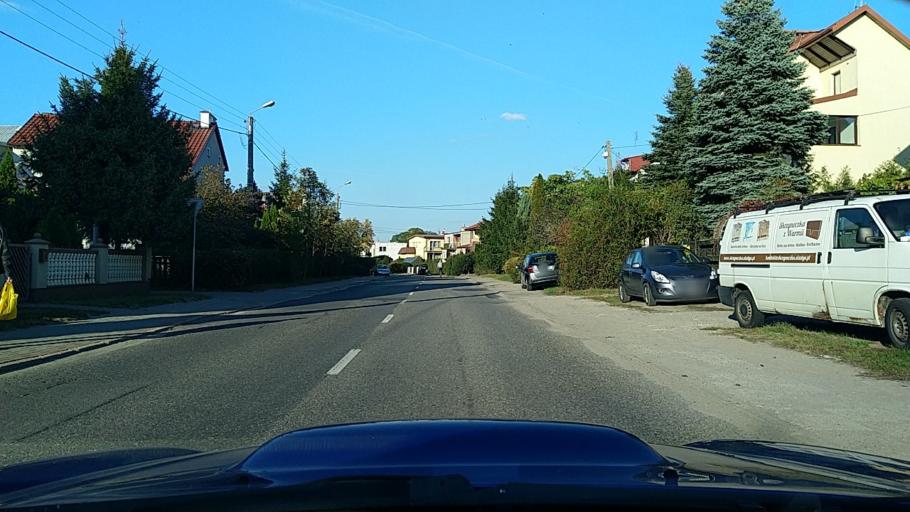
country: PL
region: Warmian-Masurian Voivodeship
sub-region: Olsztyn
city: Kortowo
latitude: 53.7659
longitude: 20.4175
